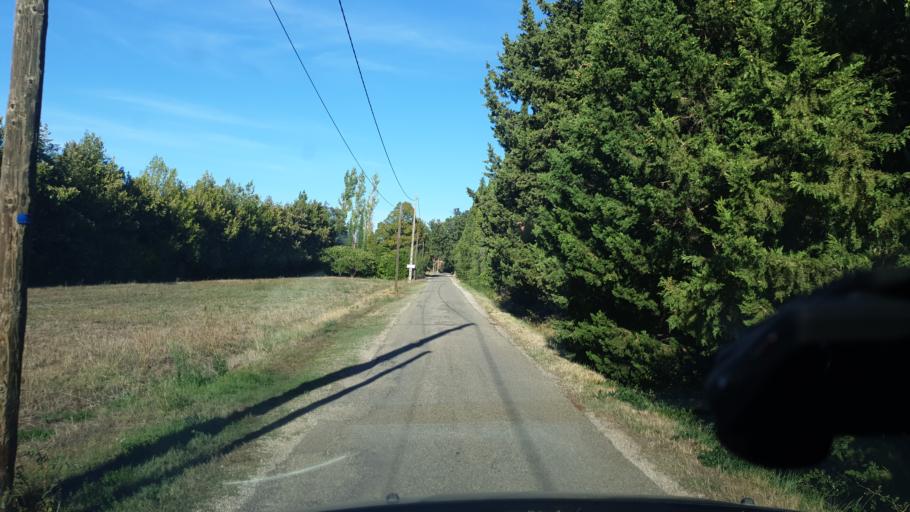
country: FR
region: Provence-Alpes-Cote d'Azur
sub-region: Departement du Vaucluse
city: Monteux
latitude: 44.0470
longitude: 5.0139
